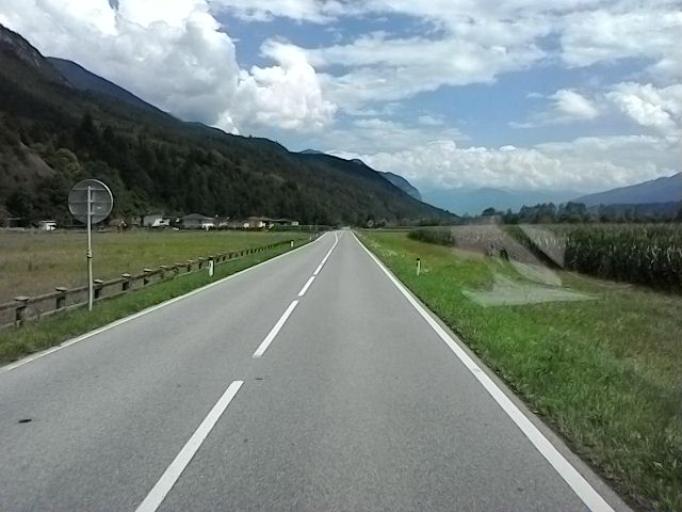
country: AT
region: Tyrol
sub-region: Politischer Bezirk Innsbruck Land
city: Hatting
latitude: 47.2884
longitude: 11.1714
